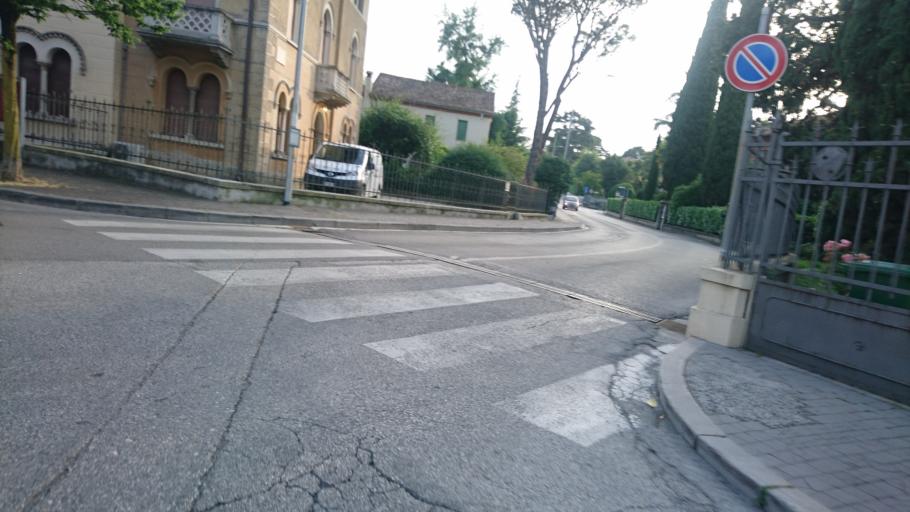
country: IT
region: Veneto
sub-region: Provincia di Treviso
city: Conegliano
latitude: 45.8847
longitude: 12.2941
